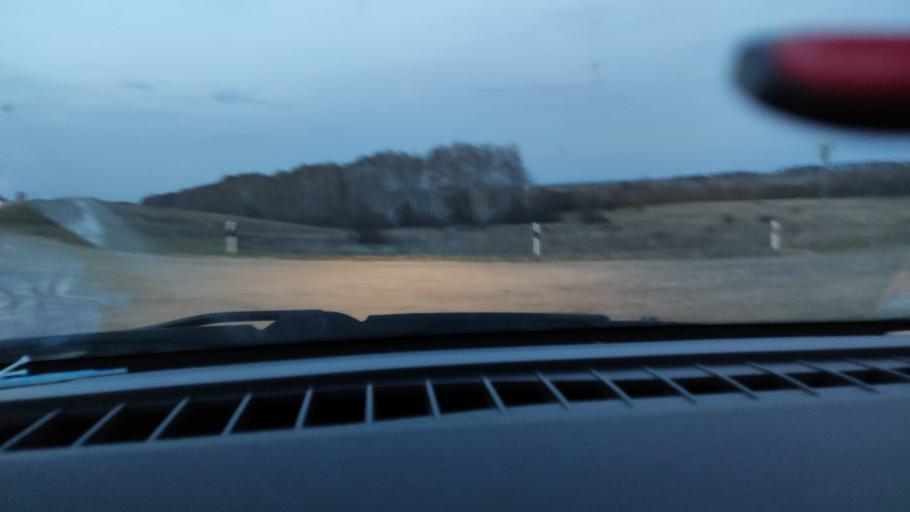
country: RU
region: Saratov
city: Sinodskoye
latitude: 52.0679
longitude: 46.7722
